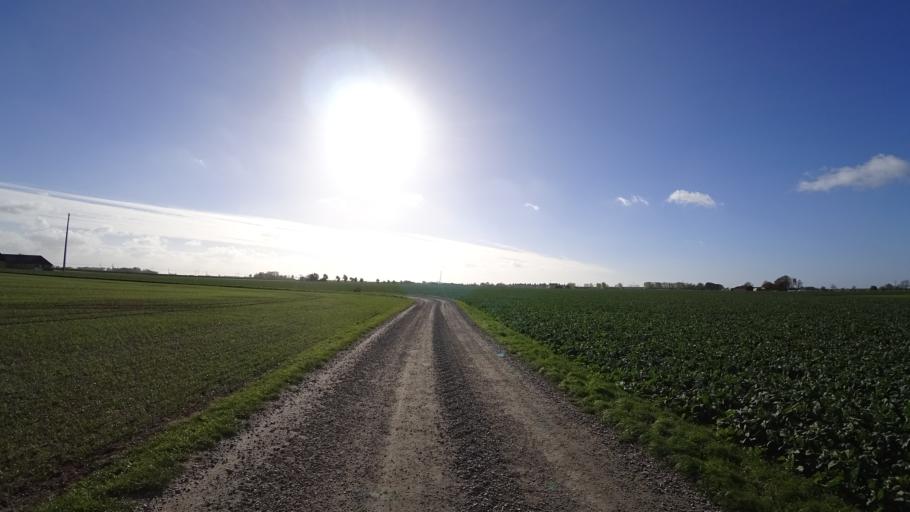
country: SE
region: Skane
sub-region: Staffanstorps Kommun
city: Hjaerup
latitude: 55.6856
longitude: 13.1442
